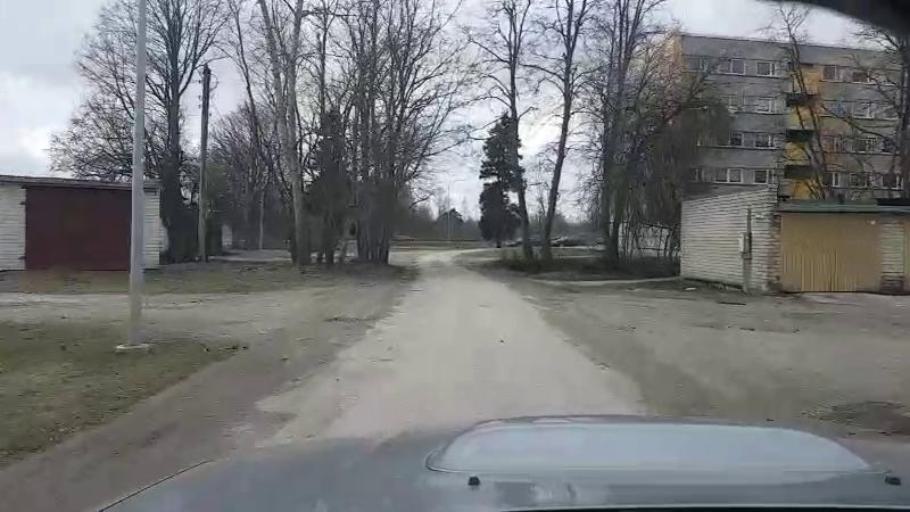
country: EE
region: Jaervamaa
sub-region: Paide linn
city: Paide
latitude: 58.8834
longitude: 25.5370
